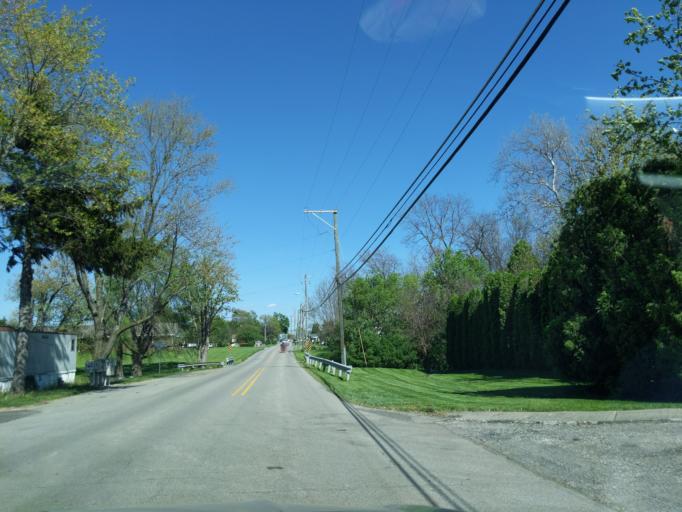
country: US
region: Indiana
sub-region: Decatur County
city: Greensburg
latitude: 39.3292
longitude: -85.4924
